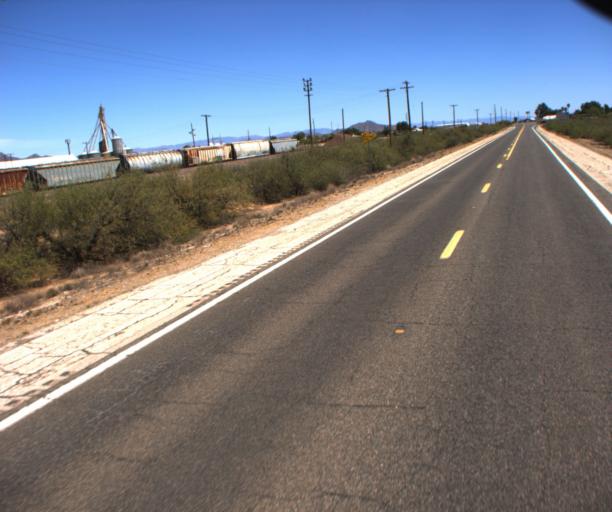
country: US
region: Arizona
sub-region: Yavapai County
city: Congress
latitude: 33.9411
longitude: -113.1837
